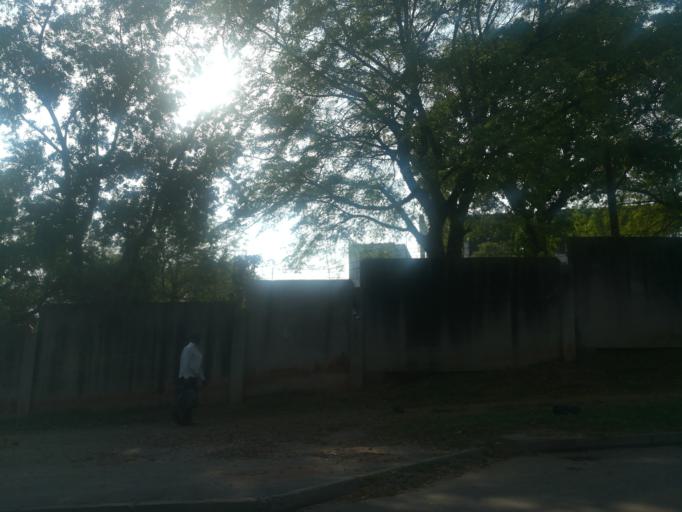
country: NG
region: Abuja Federal Capital Territory
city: Abuja
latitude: 9.0619
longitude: 7.4522
